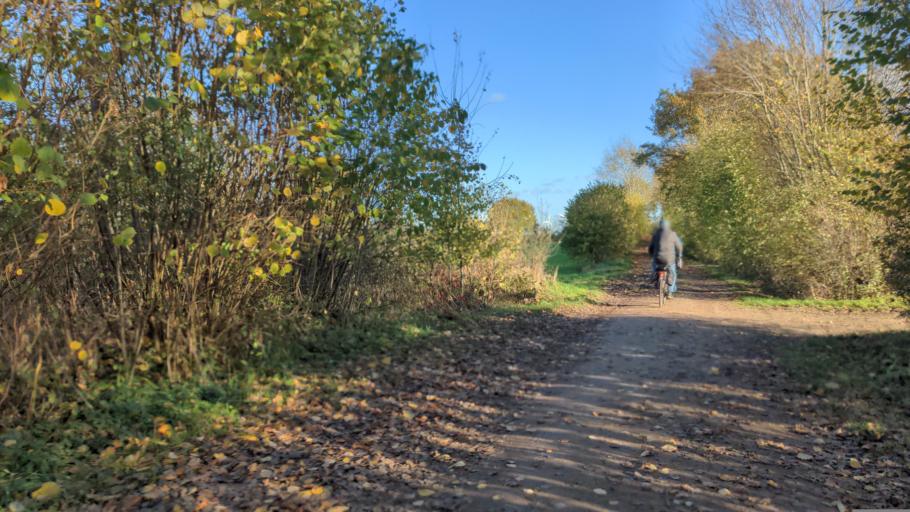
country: DE
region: Schleswig-Holstein
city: Ratekau
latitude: 53.9403
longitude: 10.7653
